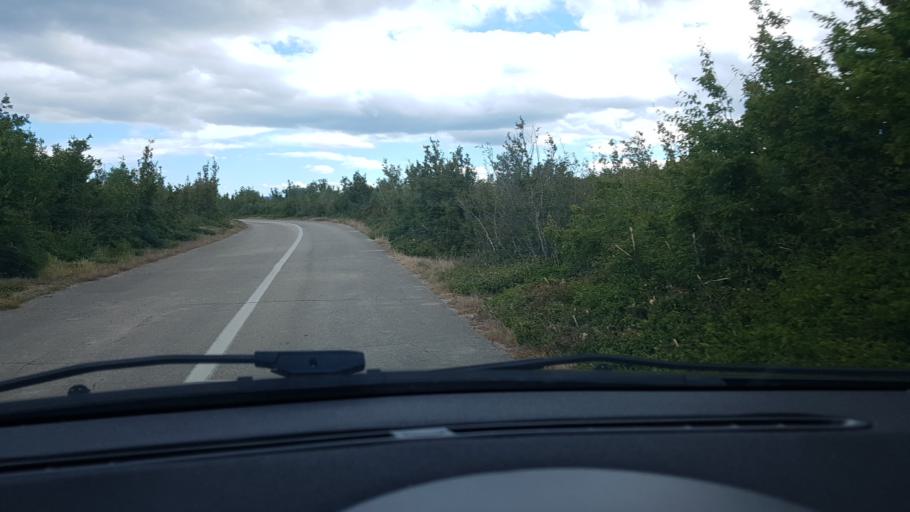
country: HR
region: Zadarska
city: Gracac
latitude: 44.1753
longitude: 15.8864
